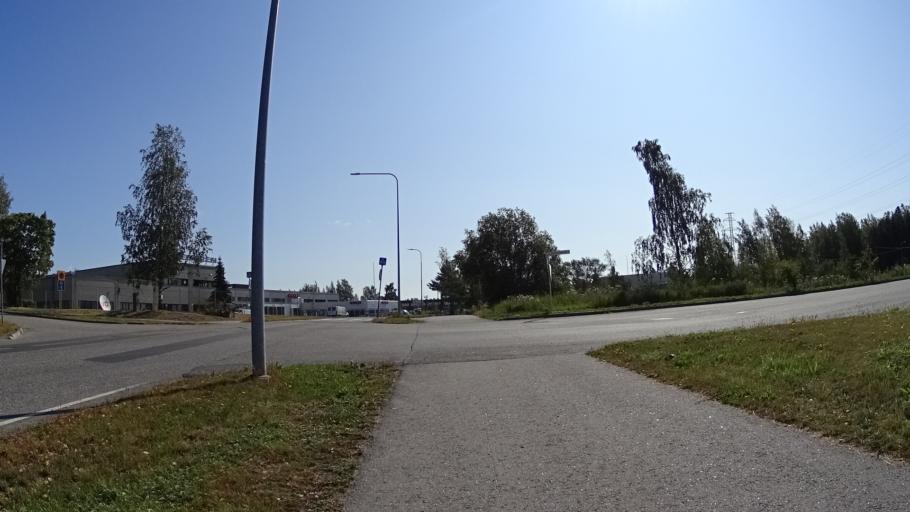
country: FI
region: Uusimaa
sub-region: Helsinki
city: Espoo
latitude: 60.1850
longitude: 24.6013
